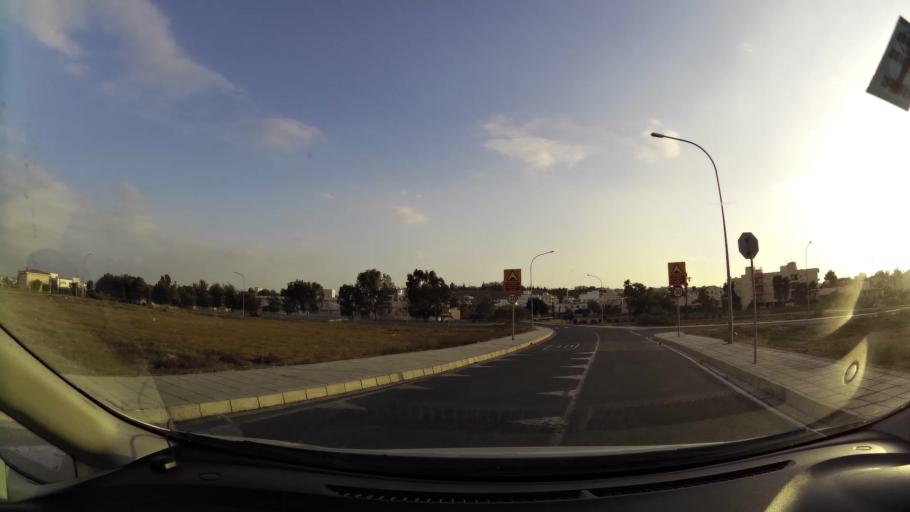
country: CY
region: Lefkosia
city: Nicosia
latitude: 35.1591
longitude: 33.4018
